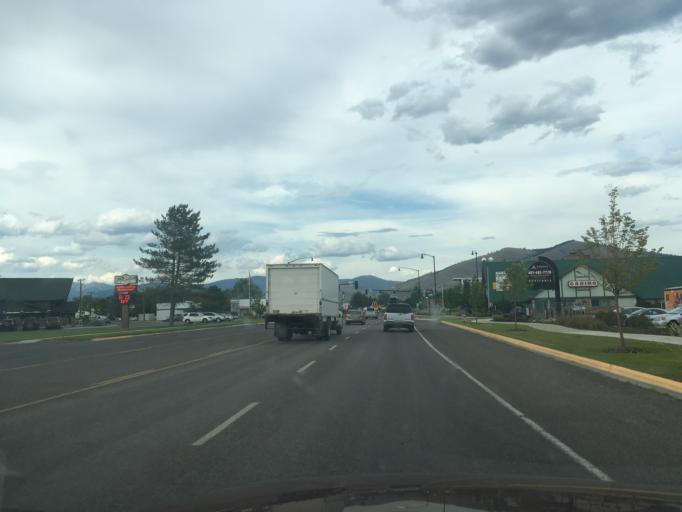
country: US
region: Montana
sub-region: Missoula County
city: Orchard Homes
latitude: 46.8372
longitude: -114.0373
